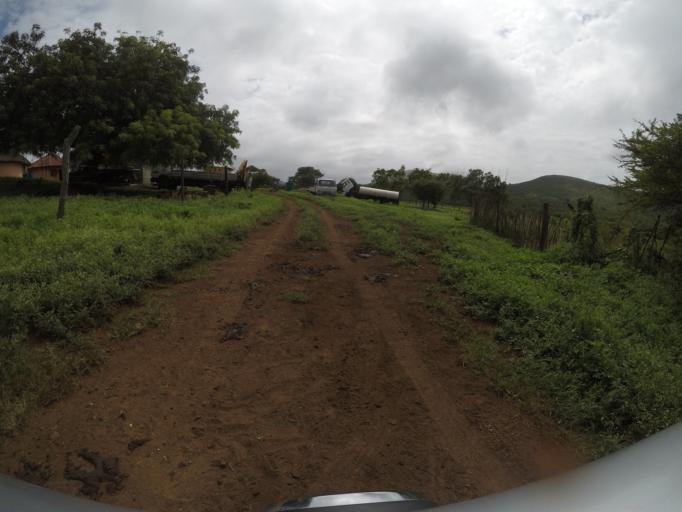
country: ZA
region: KwaZulu-Natal
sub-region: uThungulu District Municipality
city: Empangeni
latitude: -28.6207
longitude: 31.8741
